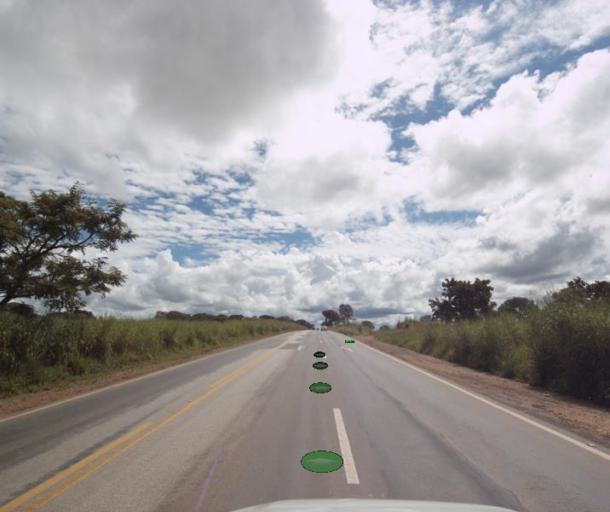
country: BR
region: Goias
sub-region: Uruacu
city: Uruacu
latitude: -14.3431
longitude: -49.1566
